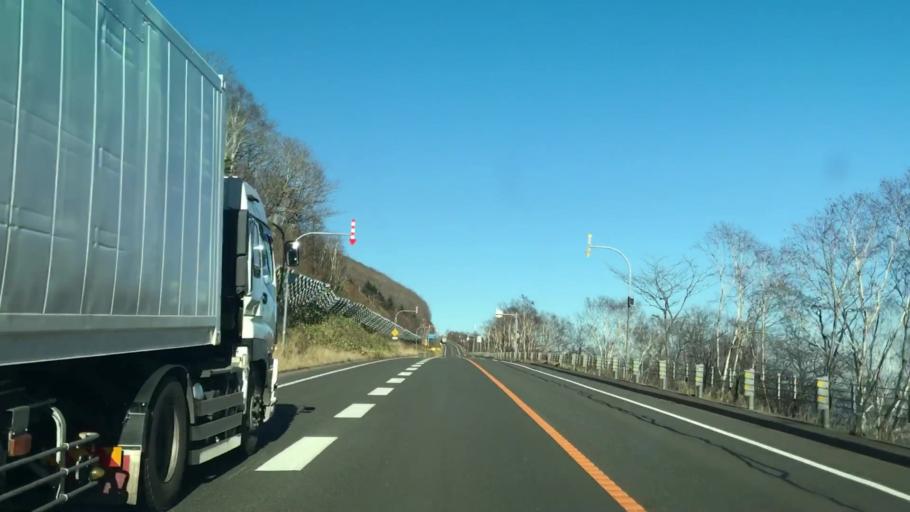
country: JP
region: Hokkaido
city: Otofuke
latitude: 42.9635
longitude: 142.7911
